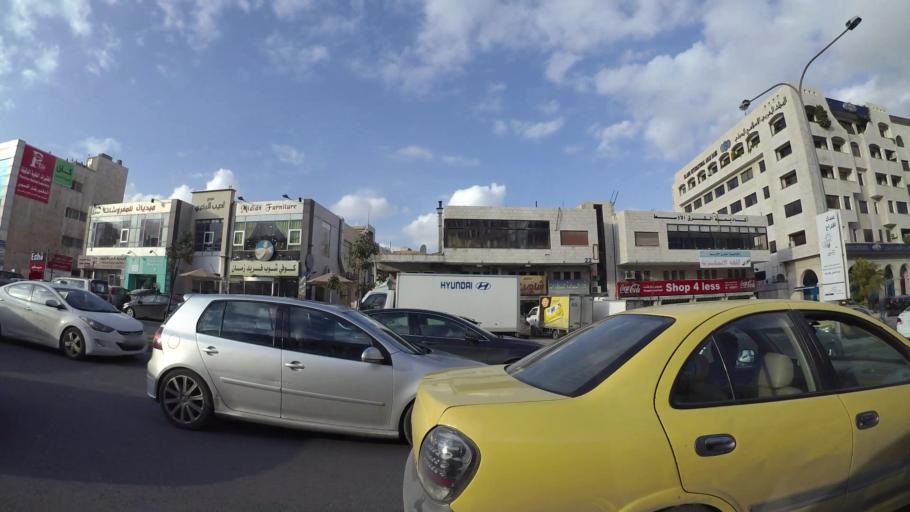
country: JO
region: Amman
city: Al Jubayhah
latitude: 31.9838
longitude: 35.8892
